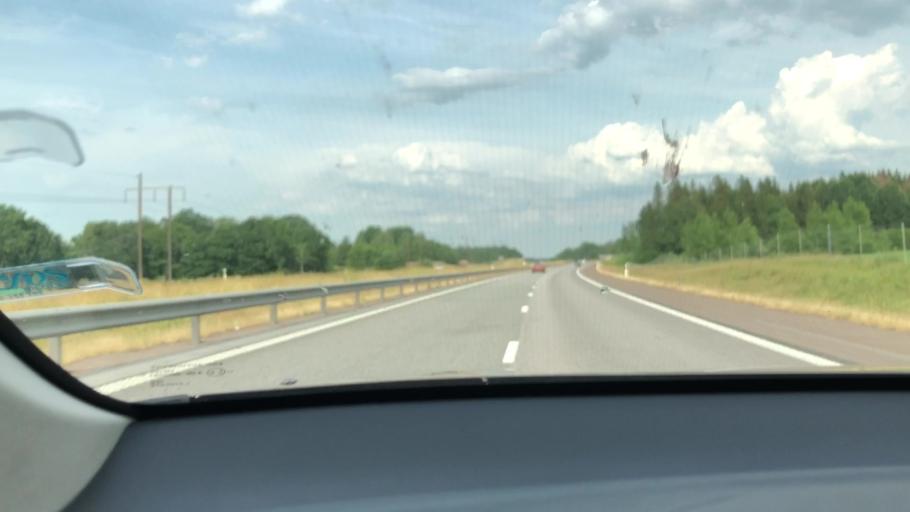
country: SE
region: OEstergoetland
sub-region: Boxholms Kommun
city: Boxholm
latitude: 58.3010
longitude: 14.9489
